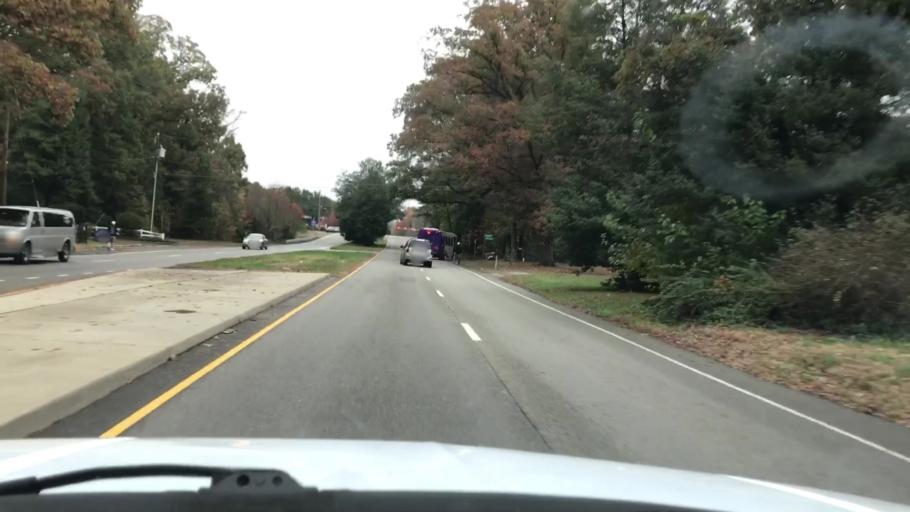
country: US
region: Virginia
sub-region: Henrico County
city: Lakeside
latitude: 37.6066
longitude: -77.4493
